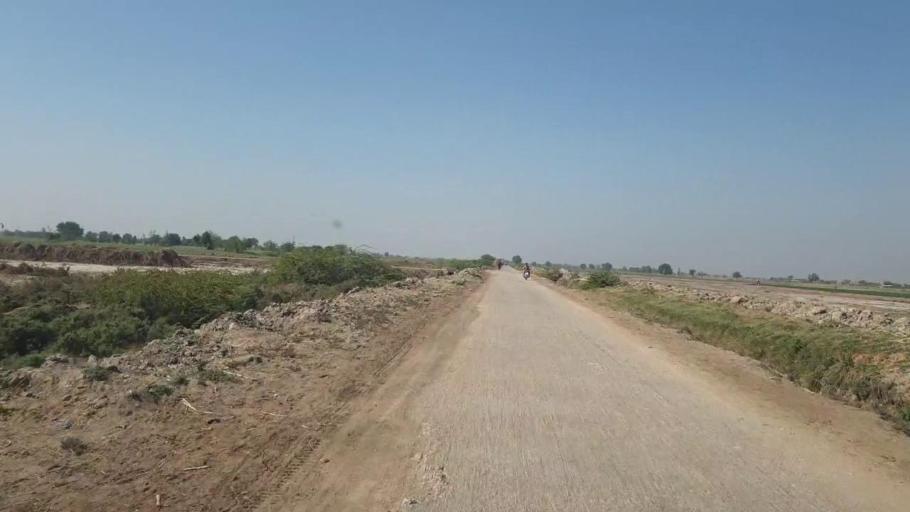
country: PK
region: Sindh
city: Samaro
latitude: 25.2787
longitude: 69.2332
